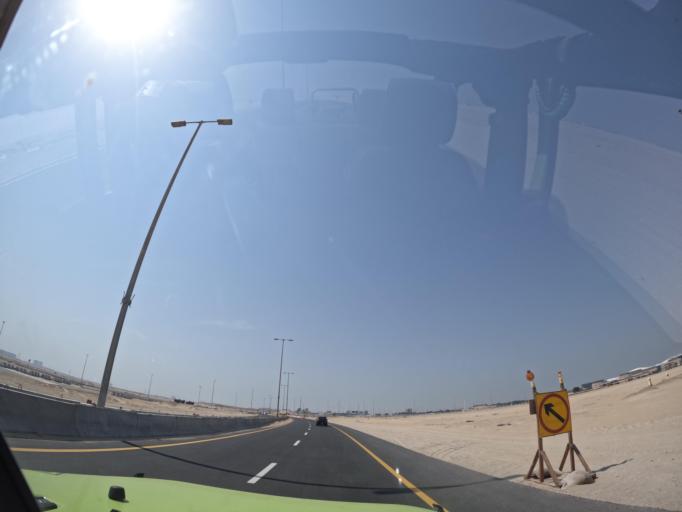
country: AE
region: Abu Dhabi
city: Abu Dhabi
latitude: 24.3858
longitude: 54.5819
